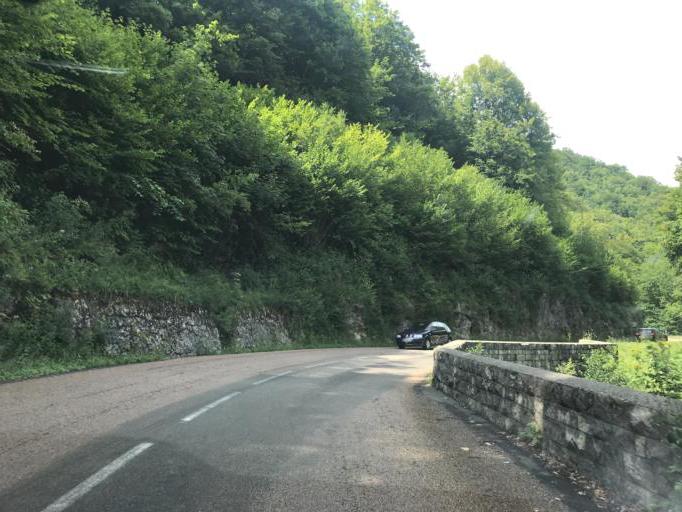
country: FR
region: Franche-Comte
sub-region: Departement du Jura
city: Valfin-les-Saint-Claude
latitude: 46.4234
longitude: 5.8581
